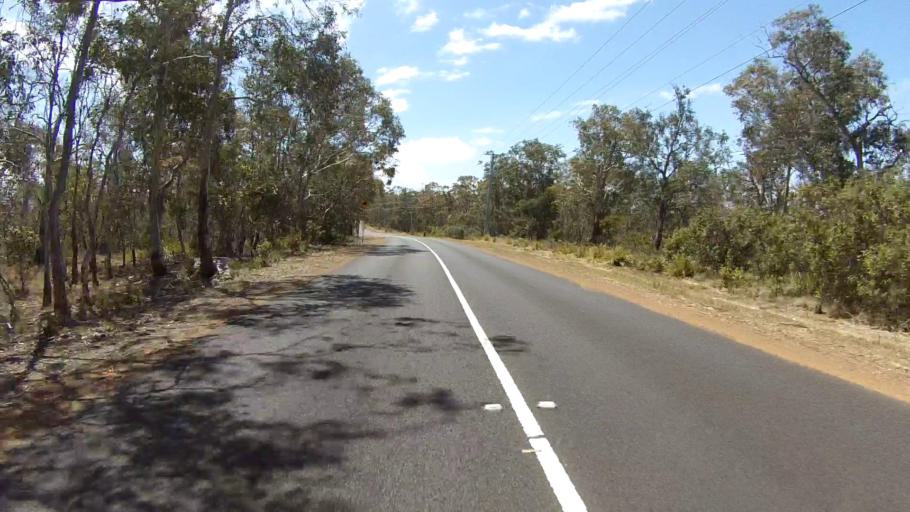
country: AU
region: Tasmania
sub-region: Clarence
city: Sandford
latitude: -43.0087
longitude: 147.4801
